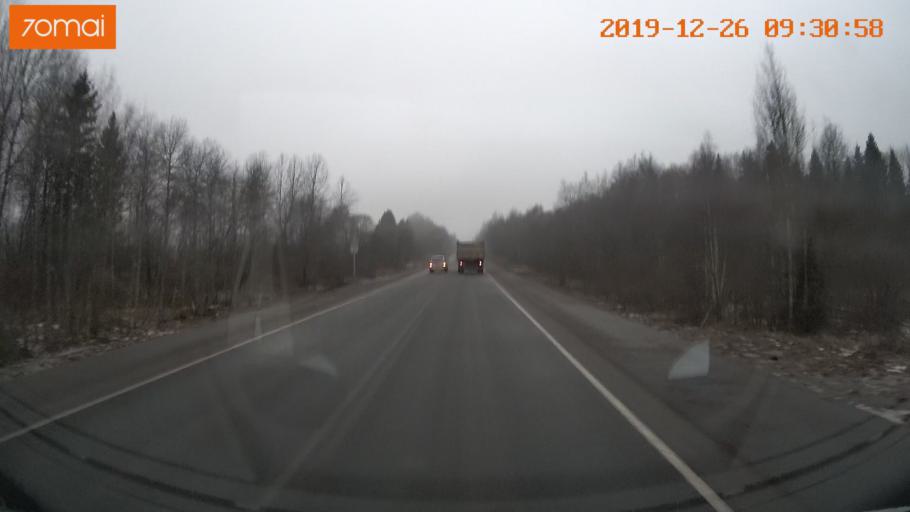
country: RU
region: Vologda
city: Gryazovets
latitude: 59.0649
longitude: 40.1335
